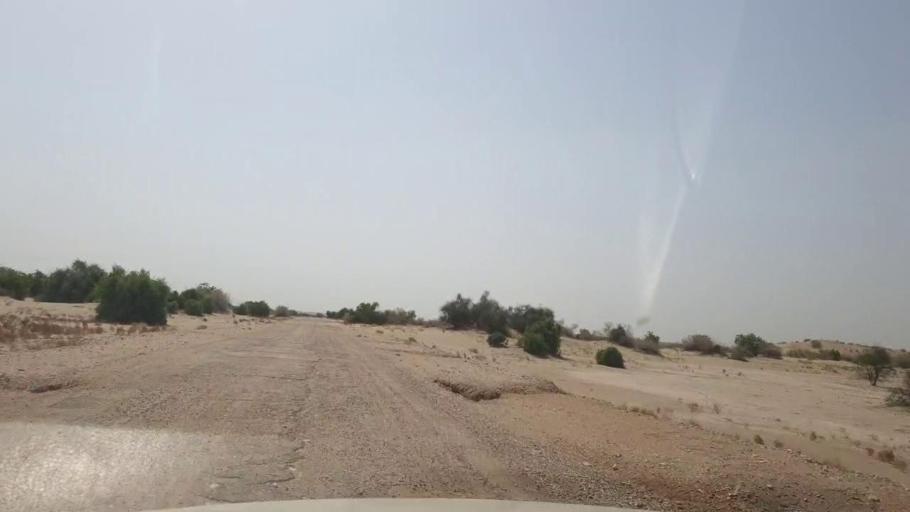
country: PK
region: Sindh
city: Rohri
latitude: 27.4331
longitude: 69.2508
